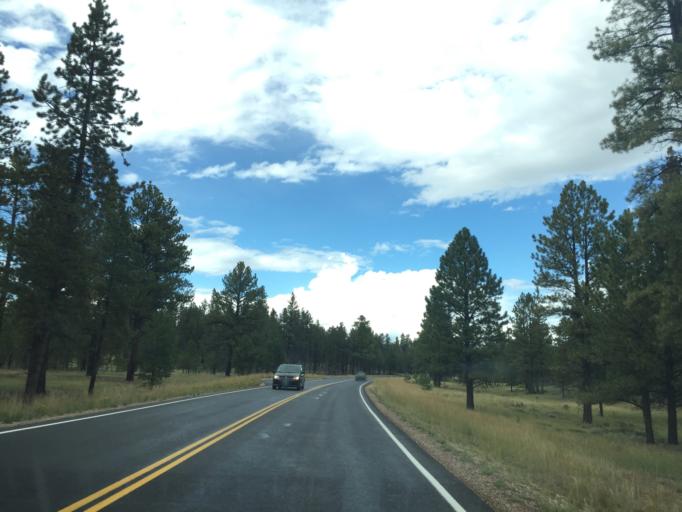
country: US
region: Utah
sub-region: Garfield County
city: Panguitch
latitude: 37.6312
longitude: -112.1737
